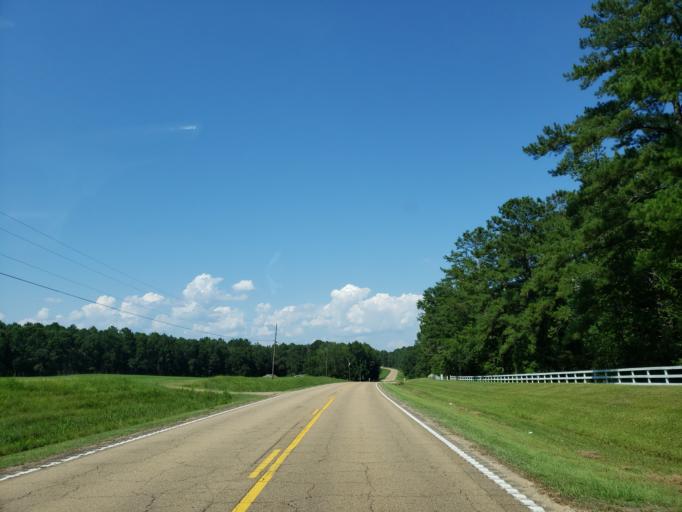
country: US
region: Mississippi
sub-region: Lamar County
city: Sumrall
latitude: 31.4346
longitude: -89.5391
